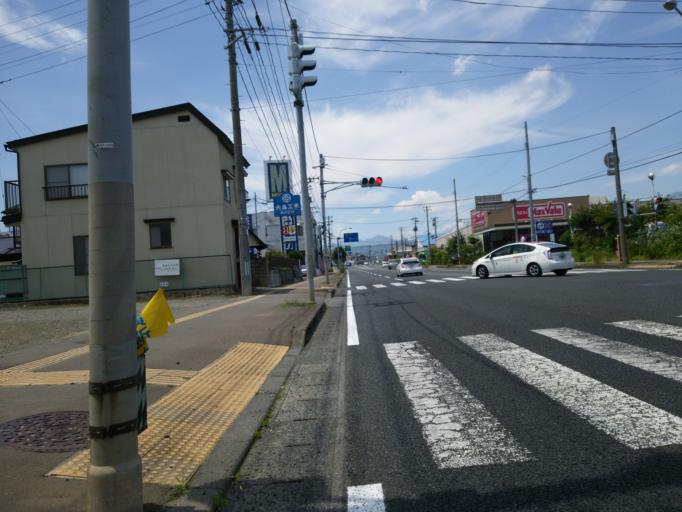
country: JP
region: Iwate
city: Morioka-shi
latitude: 39.7077
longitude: 141.1192
